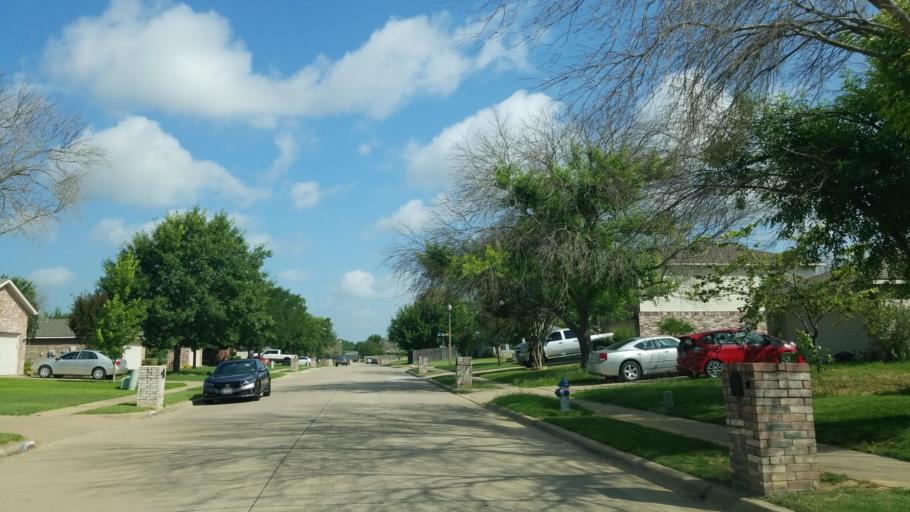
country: US
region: Texas
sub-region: Denton County
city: Copper Canyon
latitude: 33.1366
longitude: -97.1151
